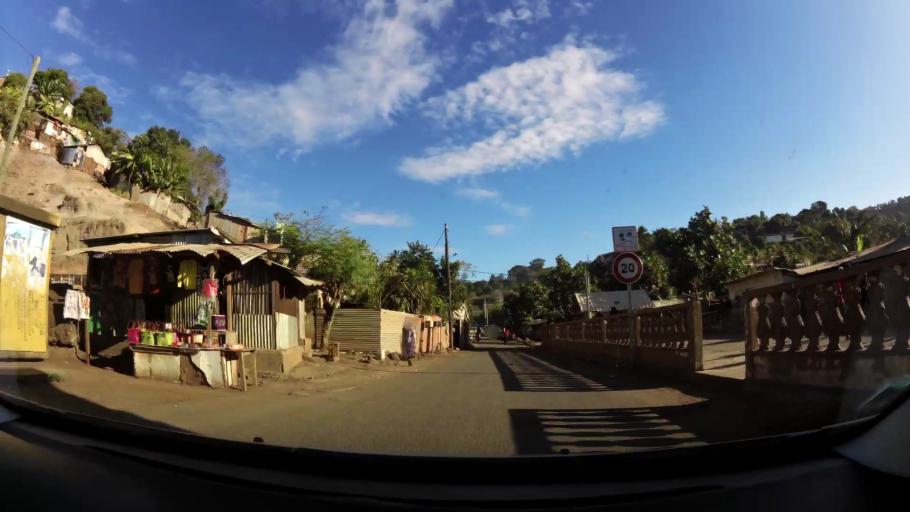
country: YT
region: Koungou
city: Koungou
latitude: -12.7450
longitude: 45.2184
